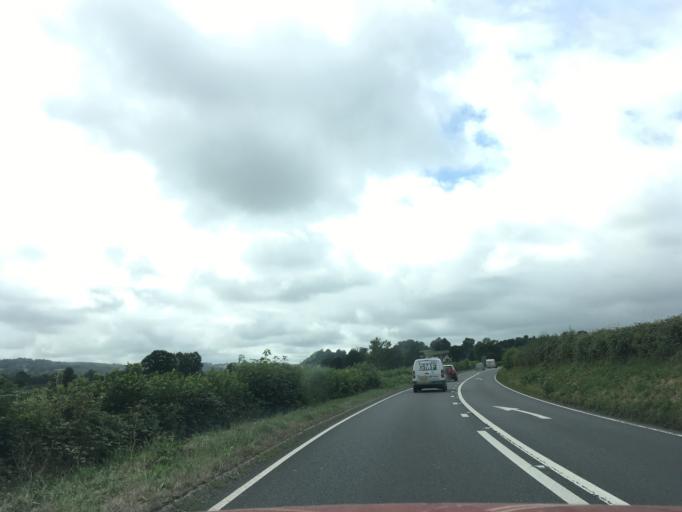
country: GB
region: Wales
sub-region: Carmarthenshire
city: Llanddarog
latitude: 51.8721
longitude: -4.1404
